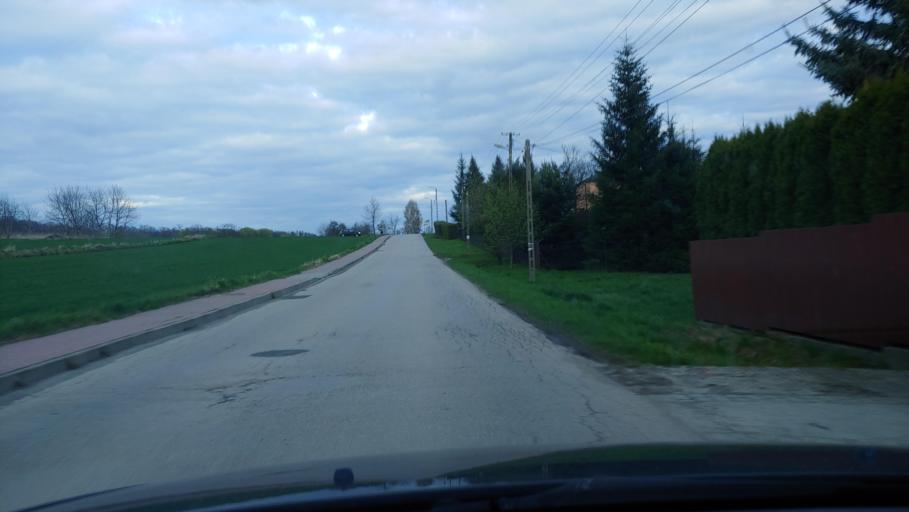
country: PL
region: Lesser Poland Voivodeship
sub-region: Powiat krakowski
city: Bolechowice
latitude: 50.1490
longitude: 19.7806
